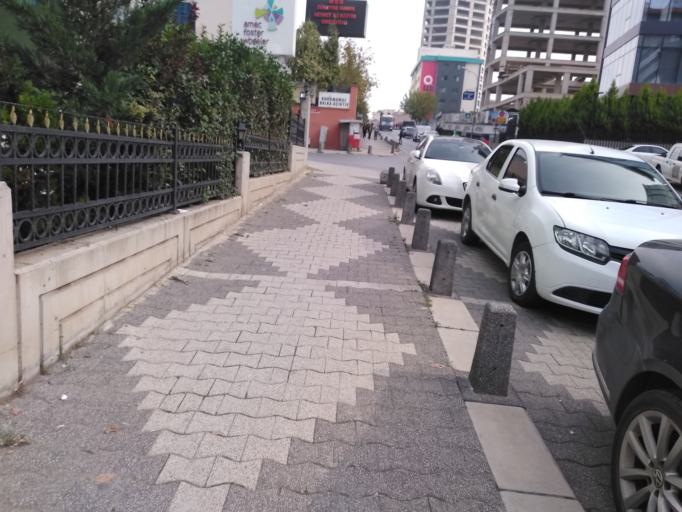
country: TR
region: Istanbul
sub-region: Atasehir
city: Atasehir
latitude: 40.9822
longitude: 29.1070
